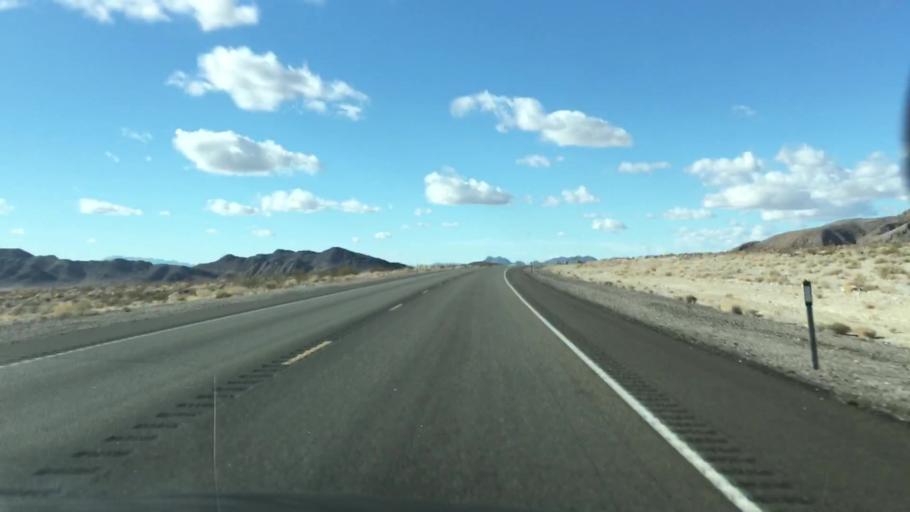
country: US
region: Nevada
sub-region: Nye County
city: Pahrump
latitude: 36.5732
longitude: -116.1830
